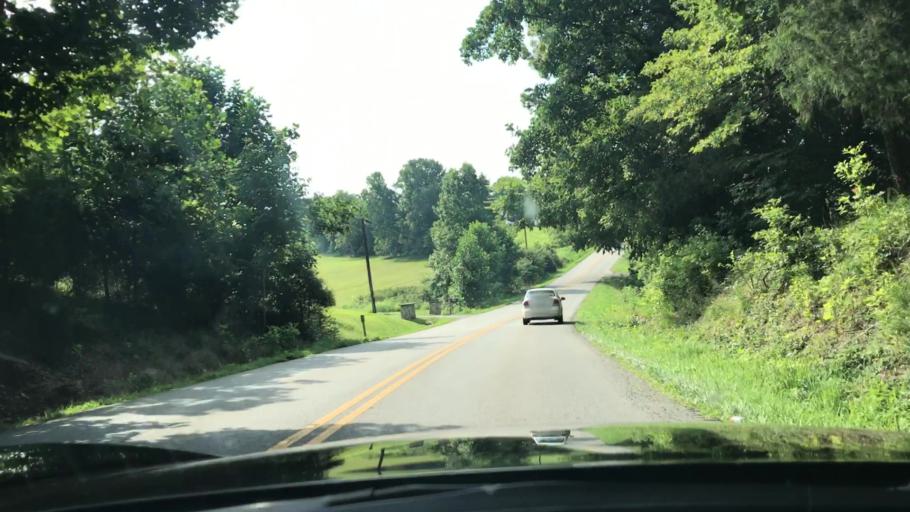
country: US
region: Kentucky
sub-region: Green County
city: Greensburg
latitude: 37.2671
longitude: -85.5636
